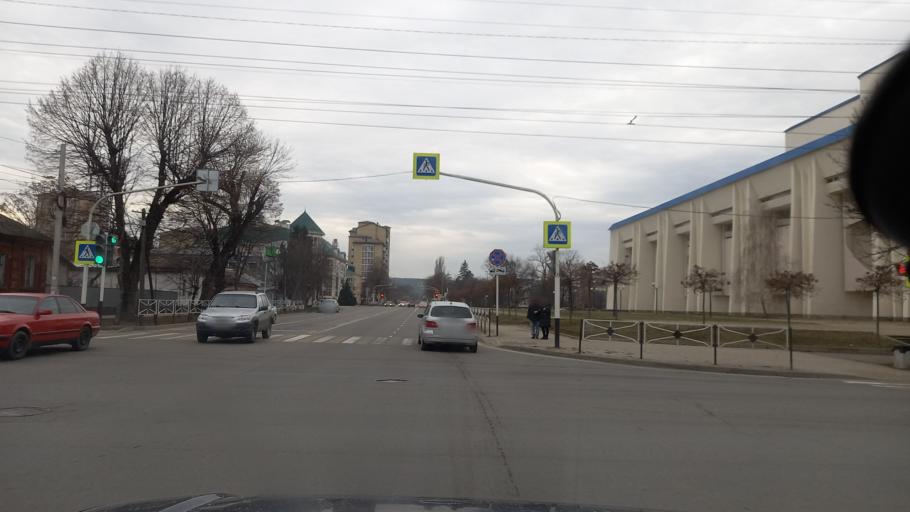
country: RU
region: Adygeya
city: Maykop
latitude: 44.6099
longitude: 40.1005
